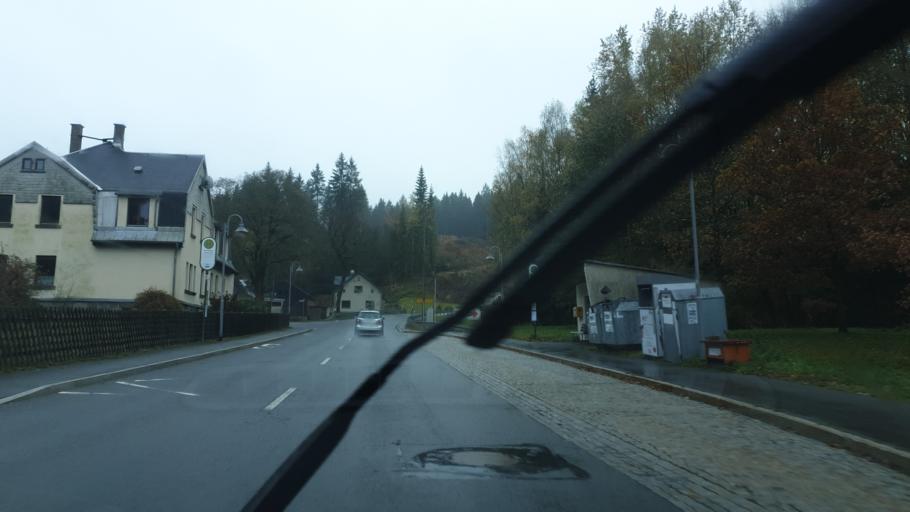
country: DE
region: Saxony
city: Tannenbergsthal
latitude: 50.4295
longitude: 12.4714
